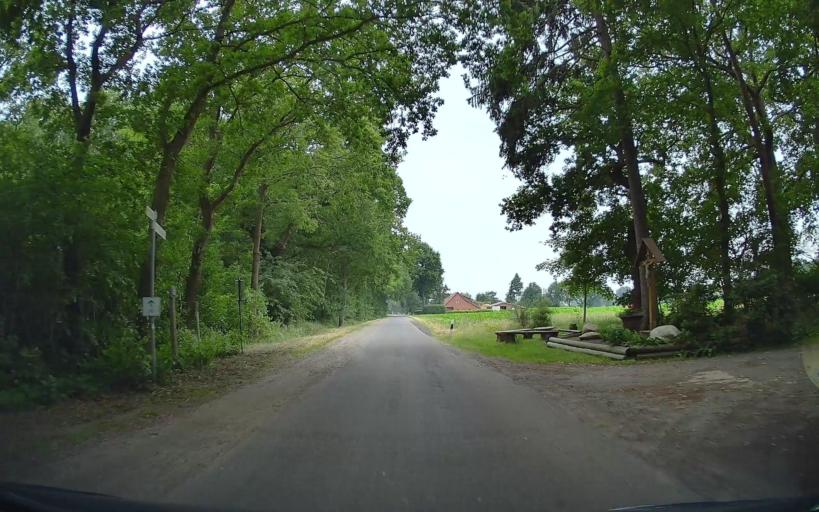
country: DE
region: Lower Saxony
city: Friesoythe
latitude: 53.0245
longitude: 7.9022
